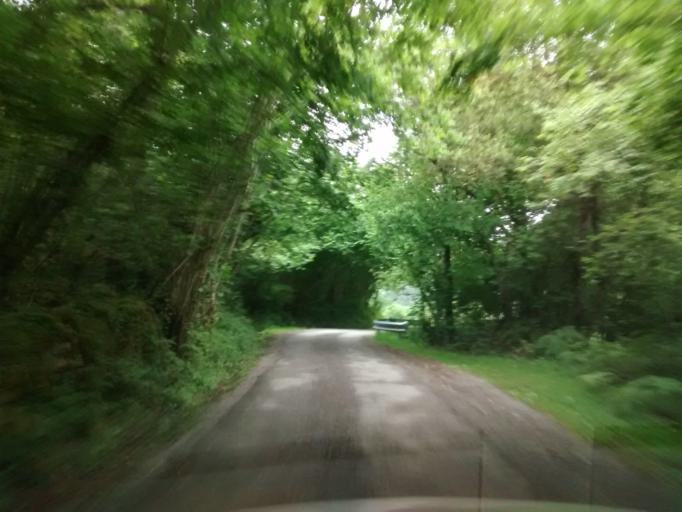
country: ES
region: Asturias
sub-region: Province of Asturias
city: Pilona
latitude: 43.2742
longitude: -5.3488
